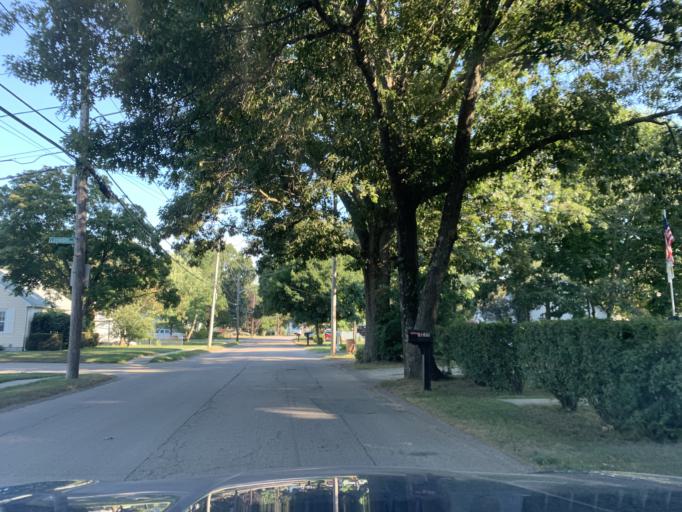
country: US
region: Rhode Island
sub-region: Kent County
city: Warwick
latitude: 41.6945
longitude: -71.4391
